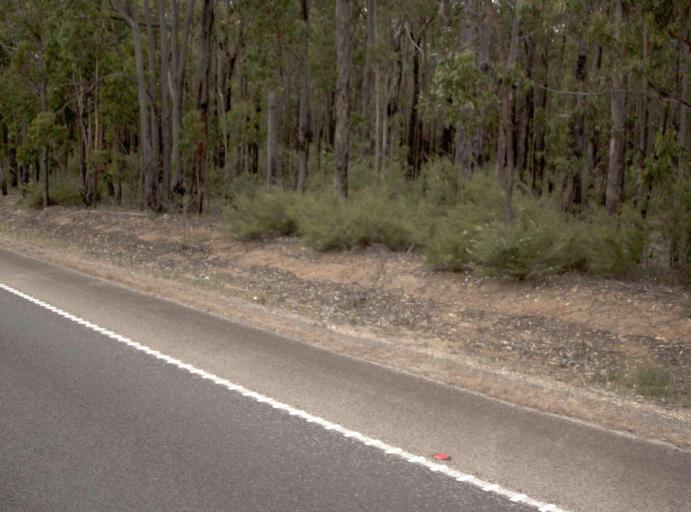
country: AU
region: Victoria
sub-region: East Gippsland
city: Lakes Entrance
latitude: -37.7148
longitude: 147.9767
